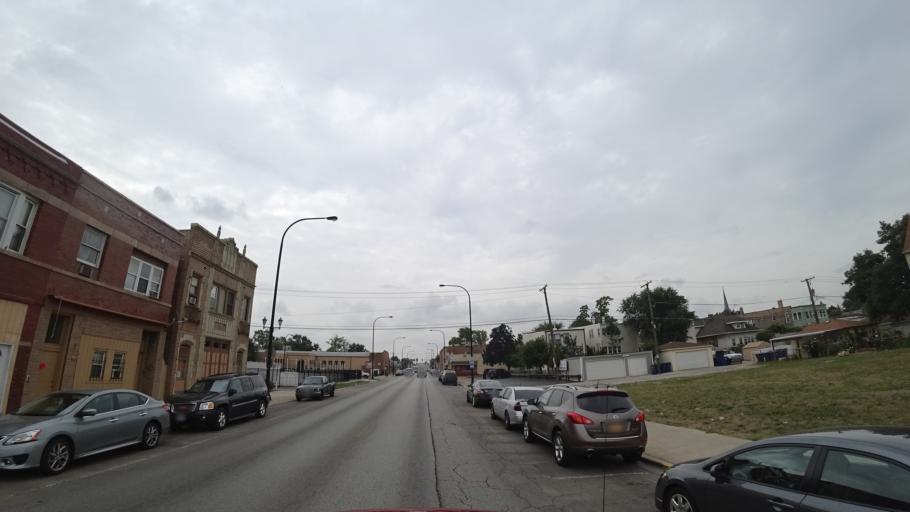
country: US
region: Illinois
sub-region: Cook County
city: Cicero
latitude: 41.8491
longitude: -87.7541
